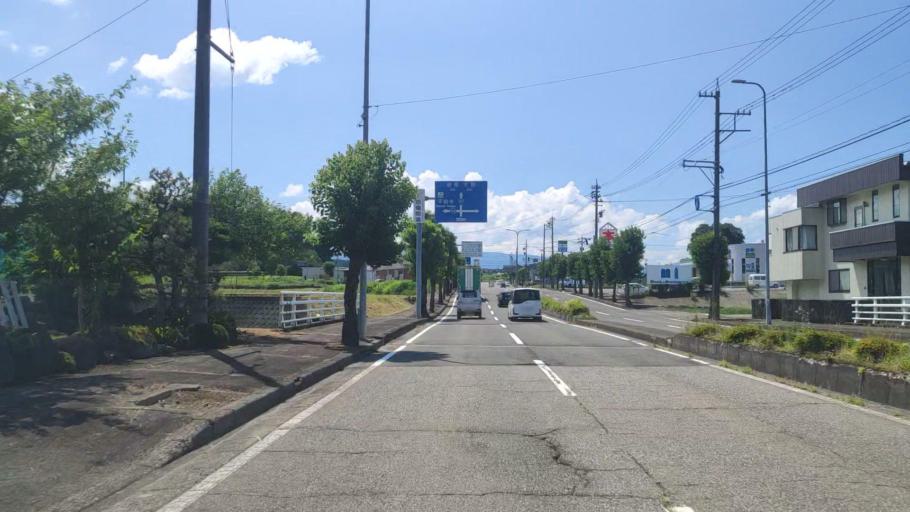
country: JP
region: Fukui
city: Katsuyama
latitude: 36.0459
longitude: 136.5167
